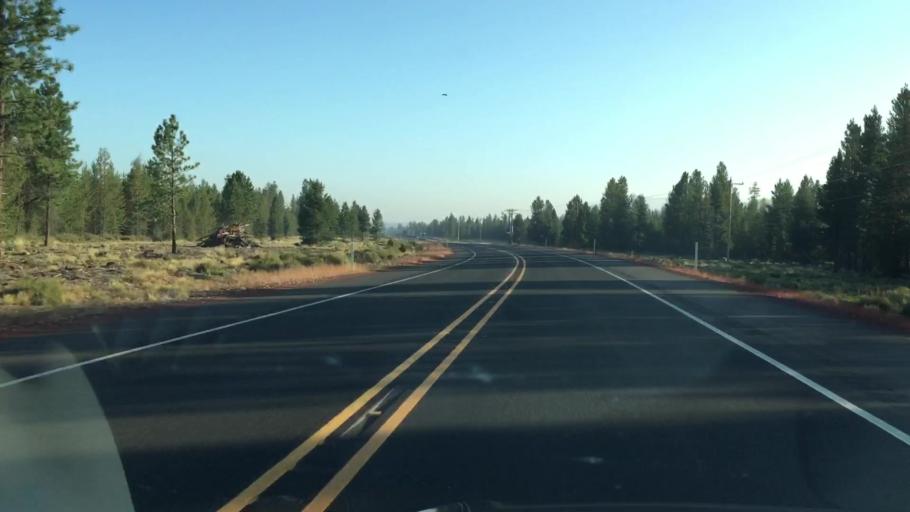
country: US
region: Oregon
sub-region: Deschutes County
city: La Pine
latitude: 43.1856
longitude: -121.7815
